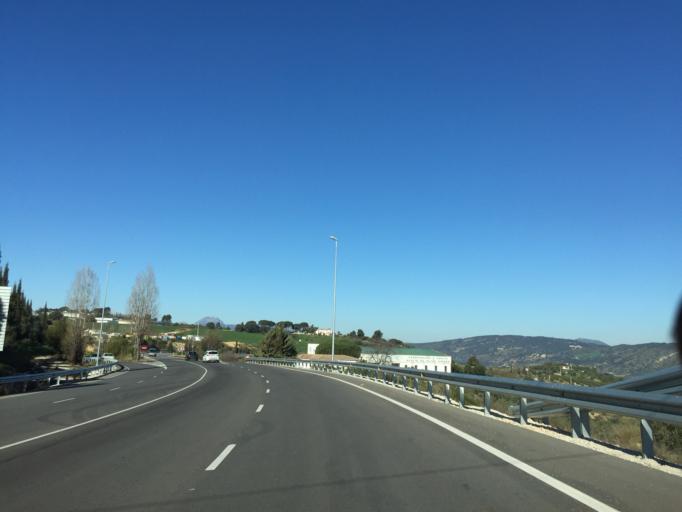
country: ES
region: Andalusia
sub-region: Provincia de Malaga
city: Ronda
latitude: 36.7551
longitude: -5.1504
